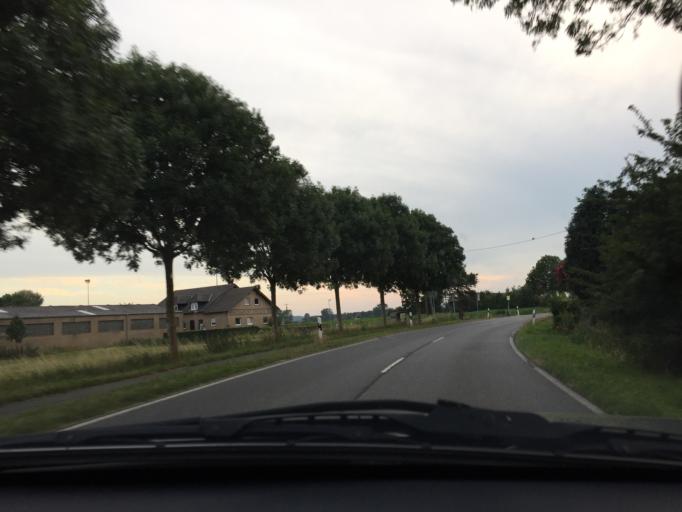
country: DE
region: North Rhine-Westphalia
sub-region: Regierungsbezirk Dusseldorf
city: Emmerich
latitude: 51.7855
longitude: 6.2070
